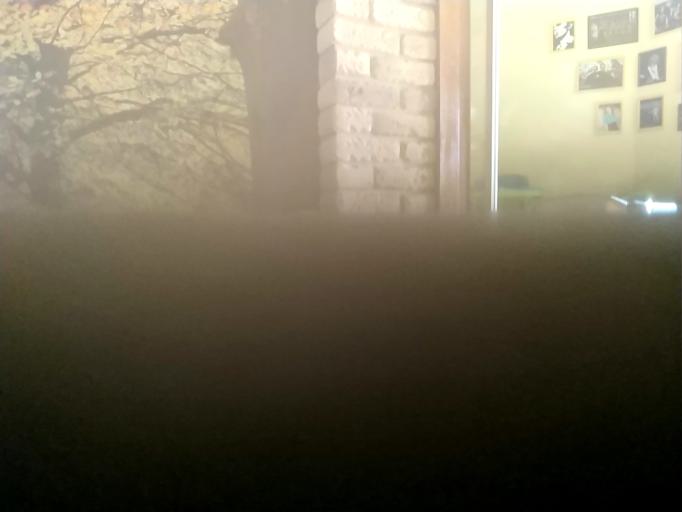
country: RU
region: Kaluga
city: Yukhnov
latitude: 54.7749
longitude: 35.0232
